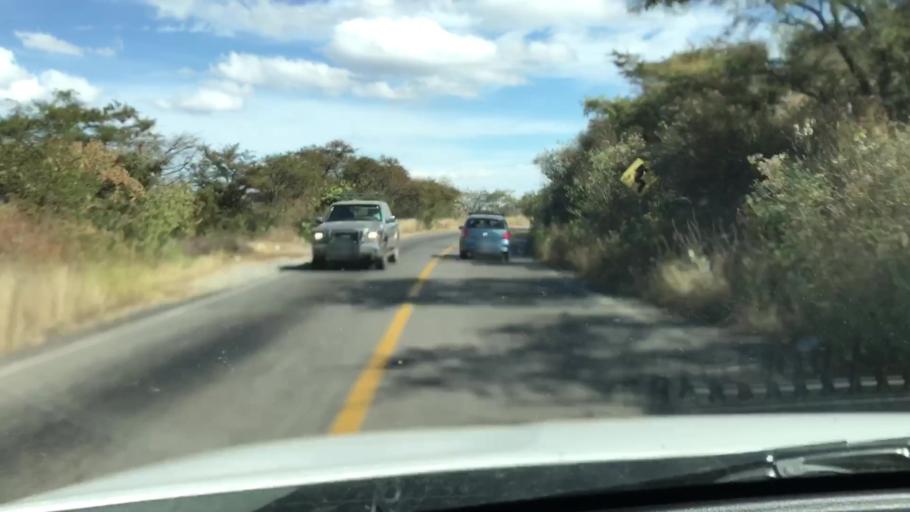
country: MX
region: Jalisco
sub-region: Zacoalco de Torres
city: Barranca de Otates (Barranca de Otatan)
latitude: 20.2017
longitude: -103.6917
